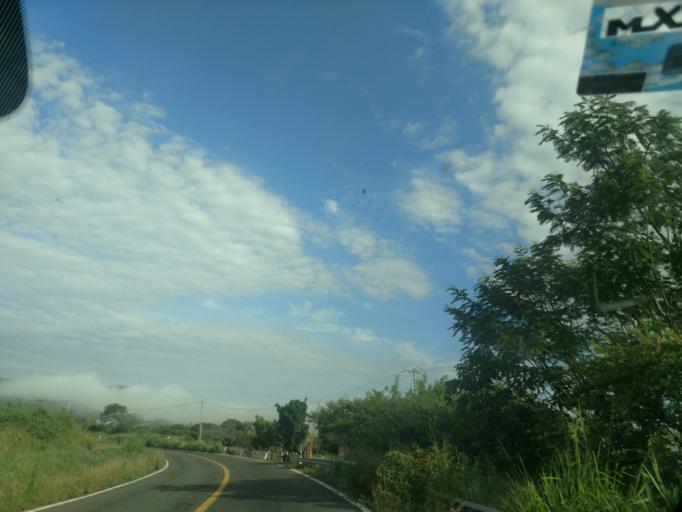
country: MX
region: Jalisco
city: Ameca
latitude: 20.5222
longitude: -104.1216
